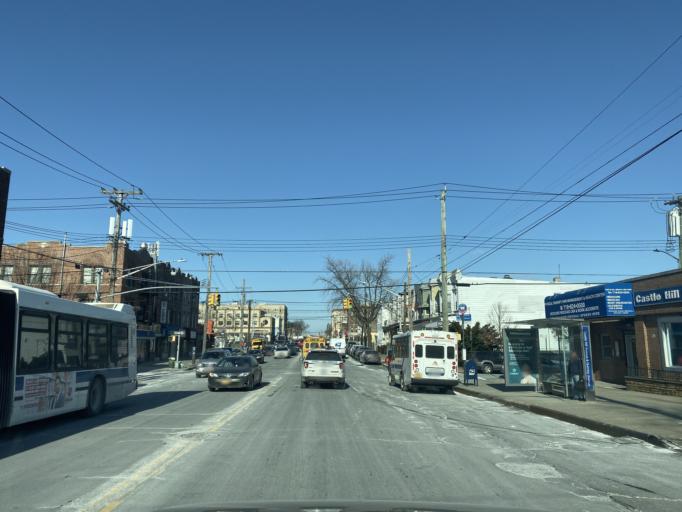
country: US
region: New York
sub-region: Bronx
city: The Bronx
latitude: 40.8258
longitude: -73.8496
